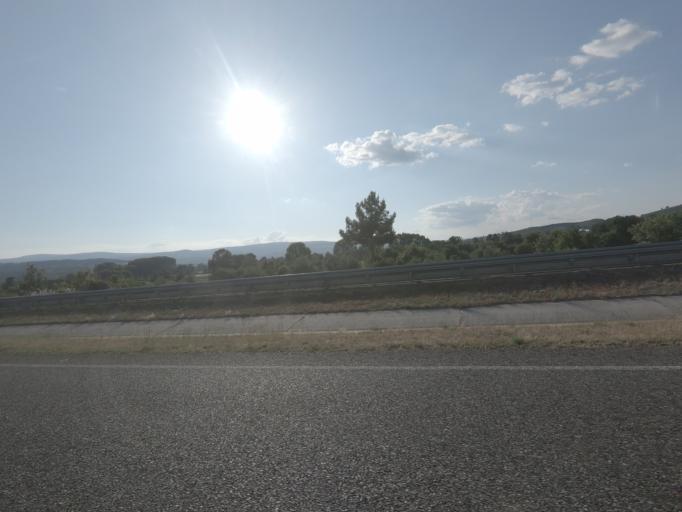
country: ES
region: Galicia
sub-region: Provincia de Ourense
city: Oimbra
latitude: 41.8429
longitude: -7.4145
